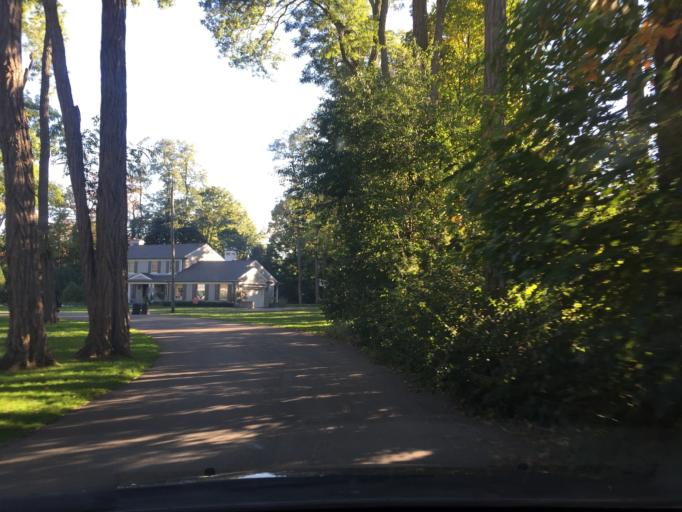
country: US
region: Michigan
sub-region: Oakland County
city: Franklin
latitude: 42.5520
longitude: -83.2919
